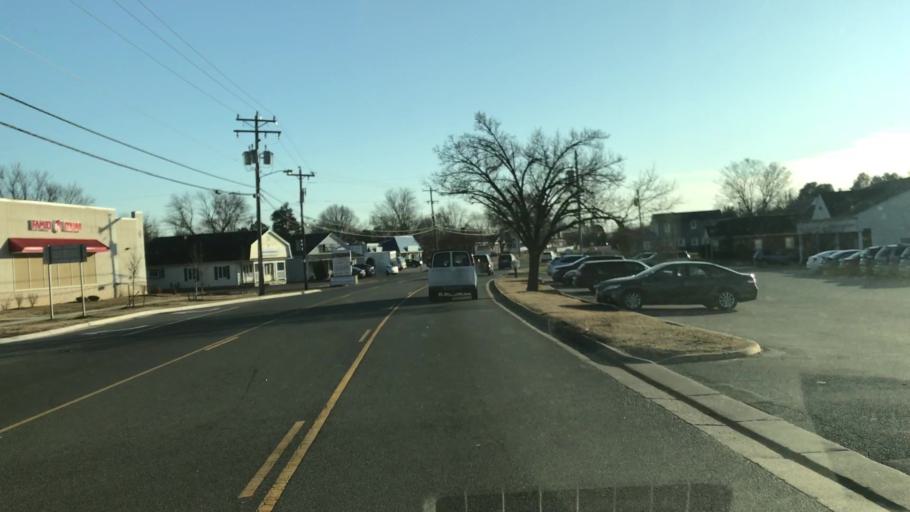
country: US
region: Virginia
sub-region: City of Fredericksburg
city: Fredericksburg
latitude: 38.2769
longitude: -77.4811
